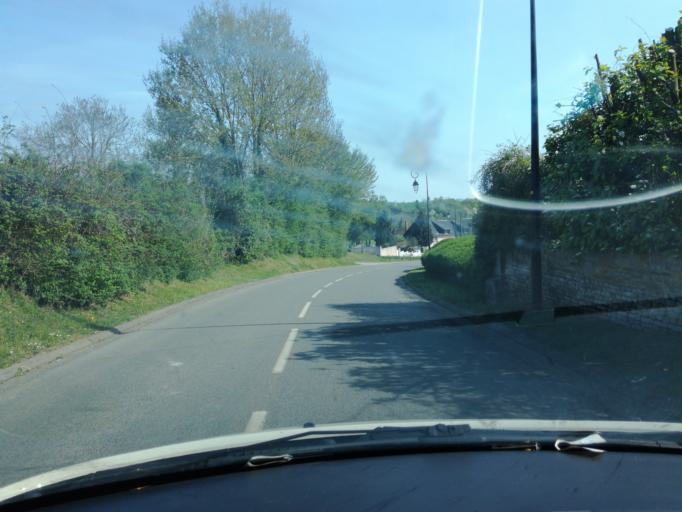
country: FR
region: Picardie
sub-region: Departement de la Somme
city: Poix-de-Picardie
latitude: 49.8218
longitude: 2.0196
